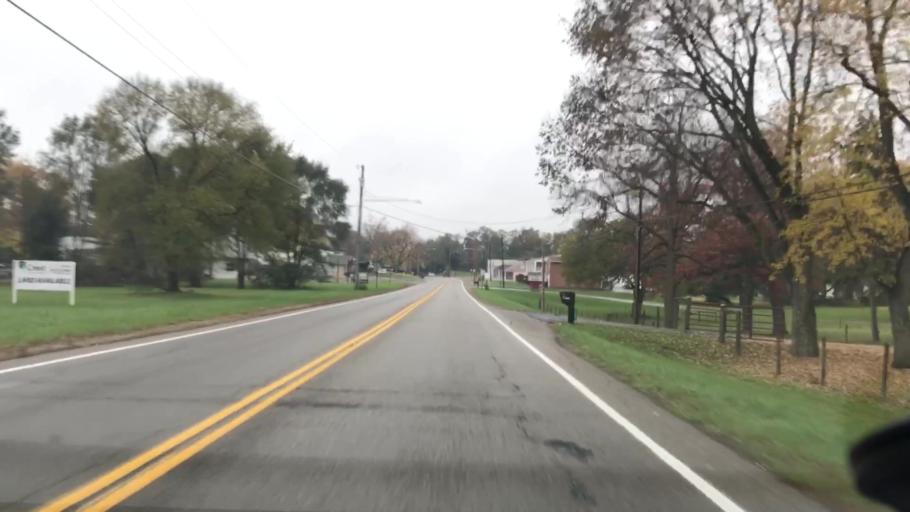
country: US
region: Ohio
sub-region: Greene County
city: Fairborn
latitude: 39.8387
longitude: -84.0066
